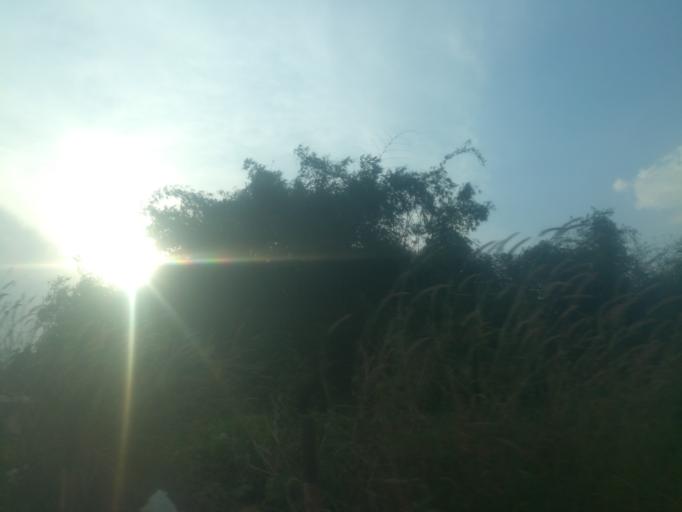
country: NG
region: Ogun
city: Abeokuta
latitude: 7.1564
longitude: 3.3107
